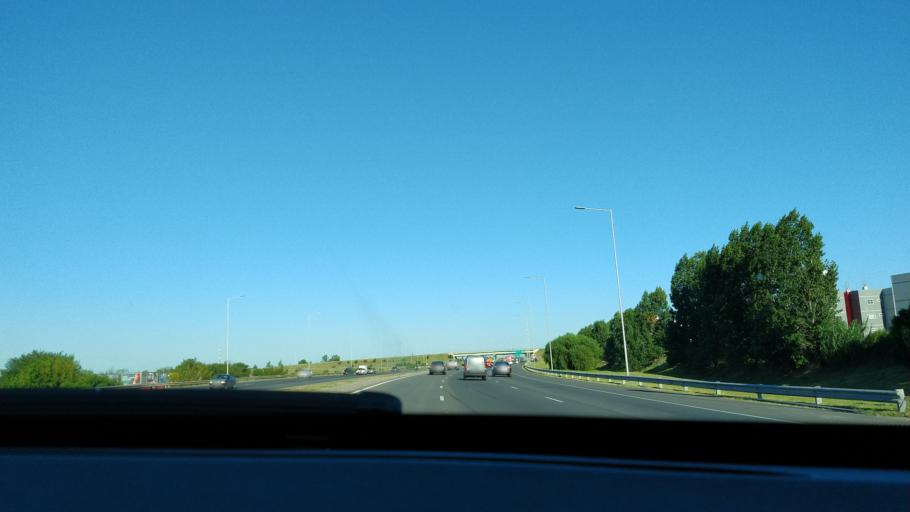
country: AR
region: Cordoba
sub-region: Departamento de Capital
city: Cordoba
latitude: -31.3535
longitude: -64.1949
